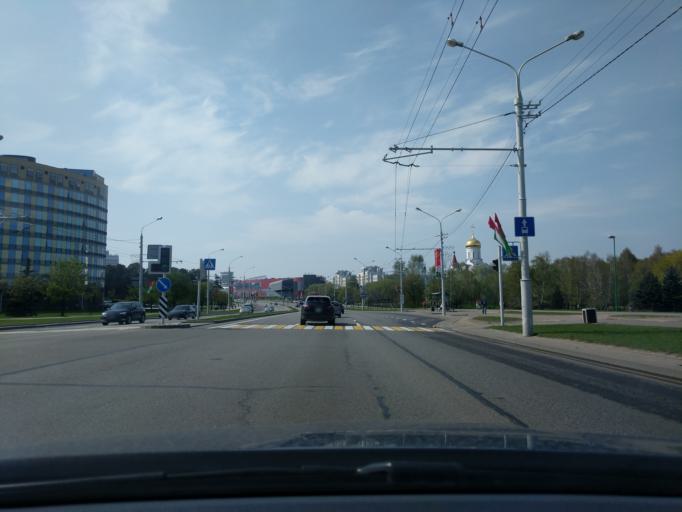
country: BY
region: Minsk
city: Novoye Medvezhino
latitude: 53.9357
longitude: 27.4977
